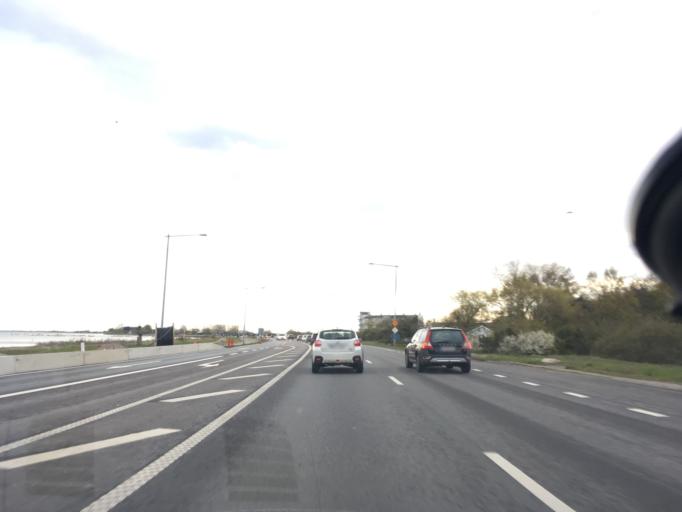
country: SE
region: Skane
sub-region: Vellinge Kommun
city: Hollviken
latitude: 55.4192
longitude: 12.9511
